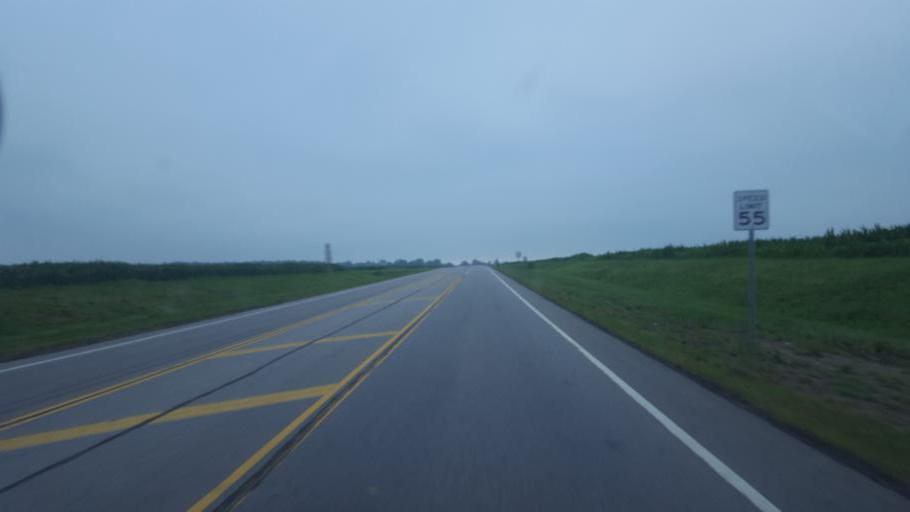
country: US
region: Ohio
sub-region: Fayette County
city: Washington Court House
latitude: 39.5628
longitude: -83.4063
